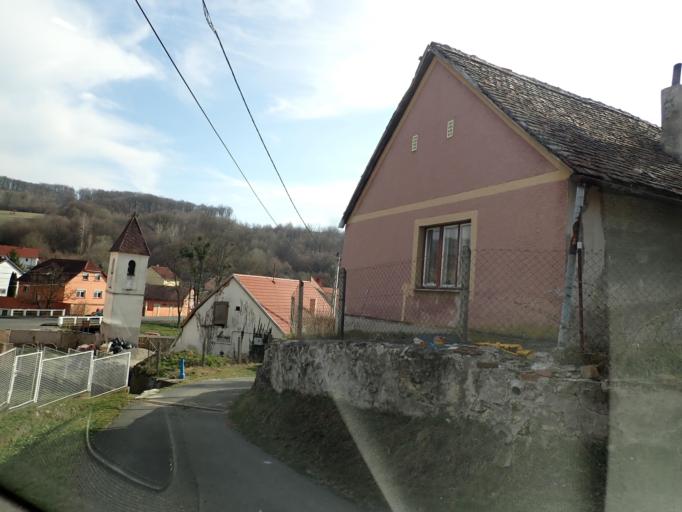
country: HU
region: Baranya
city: Komlo
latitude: 46.1636
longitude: 18.2525
